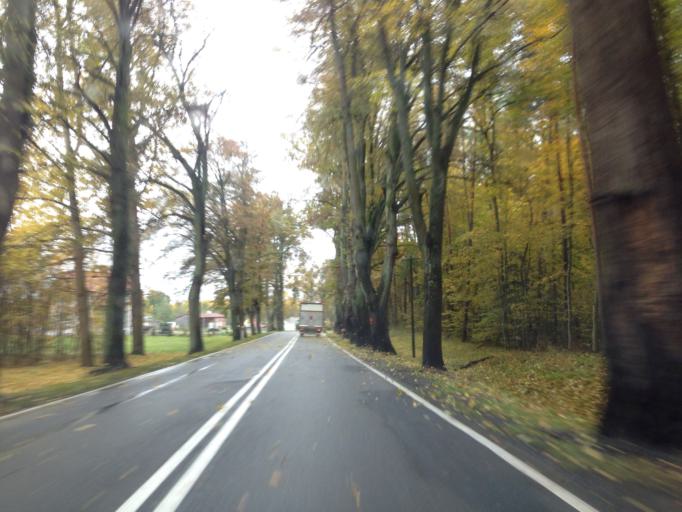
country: PL
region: Pomeranian Voivodeship
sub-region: Powiat kwidzynski
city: Ryjewo
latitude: 53.8611
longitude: 19.0014
